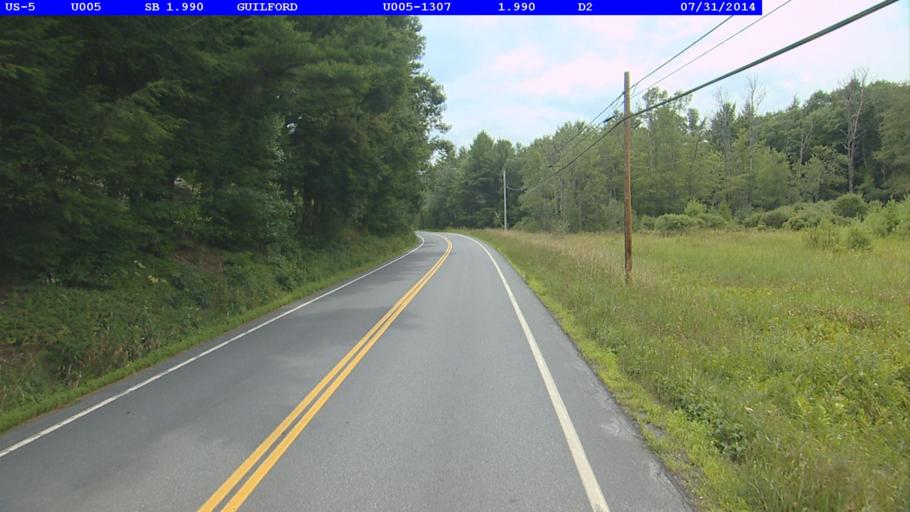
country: US
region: New Hampshire
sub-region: Cheshire County
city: Hinsdale
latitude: 42.7582
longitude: -72.5691
